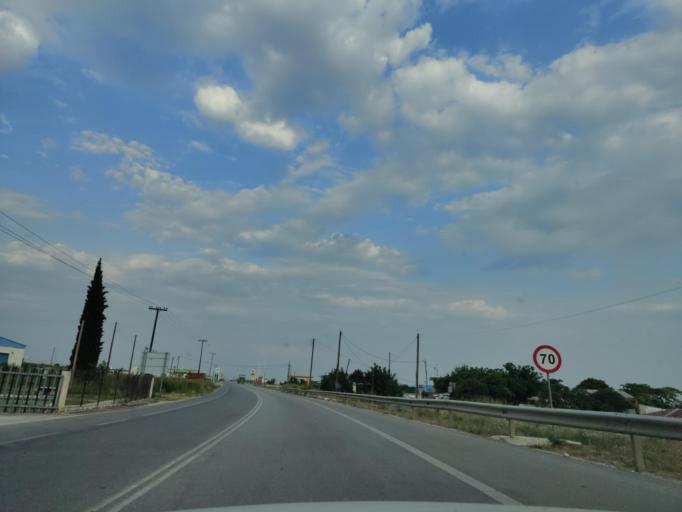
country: GR
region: East Macedonia and Thrace
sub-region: Nomos Dramas
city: Prosotsani
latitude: 41.1807
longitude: 23.9846
